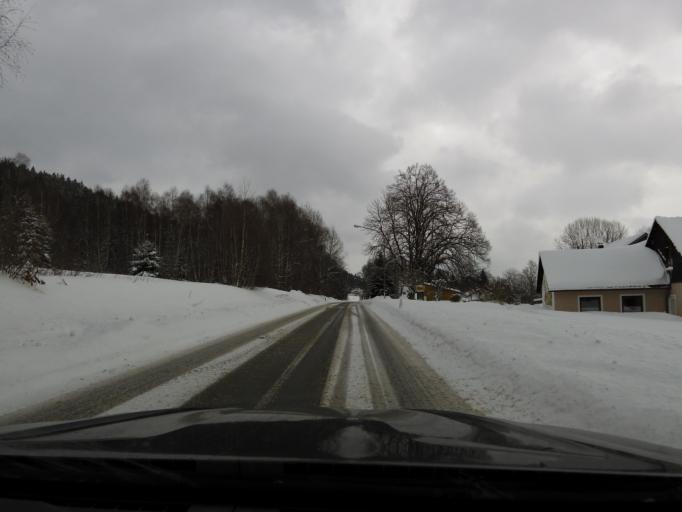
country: DE
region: Bavaria
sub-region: Lower Bavaria
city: Spiegelau
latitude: 48.9148
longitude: 13.3274
